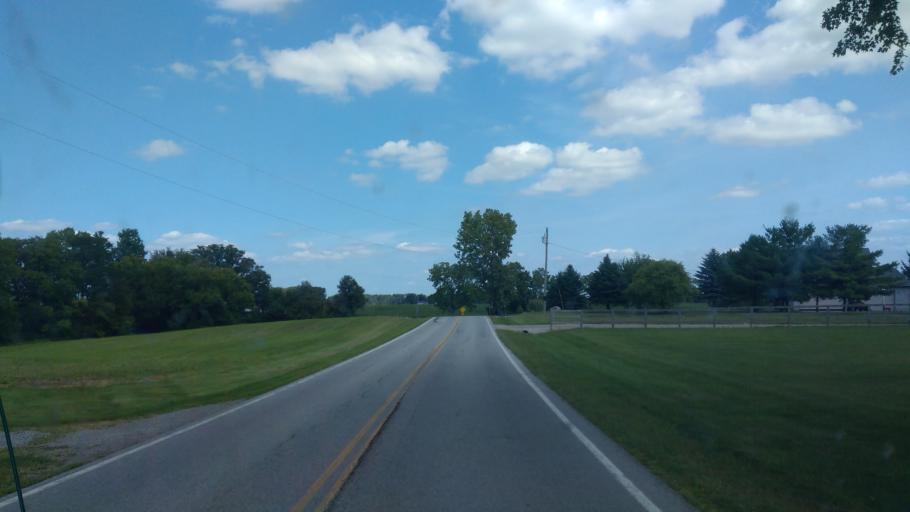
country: US
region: Ohio
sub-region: Union County
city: Richwood
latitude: 40.4353
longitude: -83.4046
